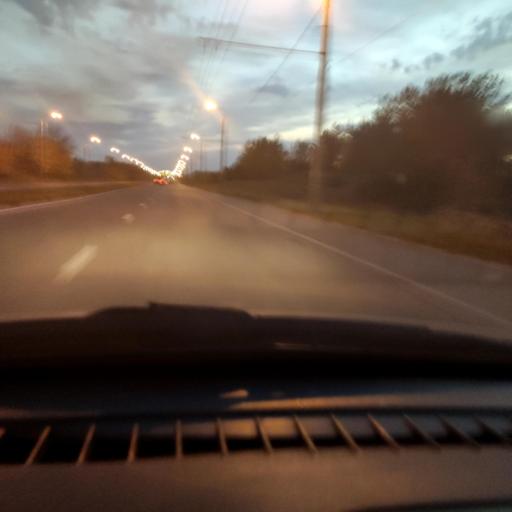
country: RU
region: Samara
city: Zhigulevsk
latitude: 53.5262
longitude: 49.5475
